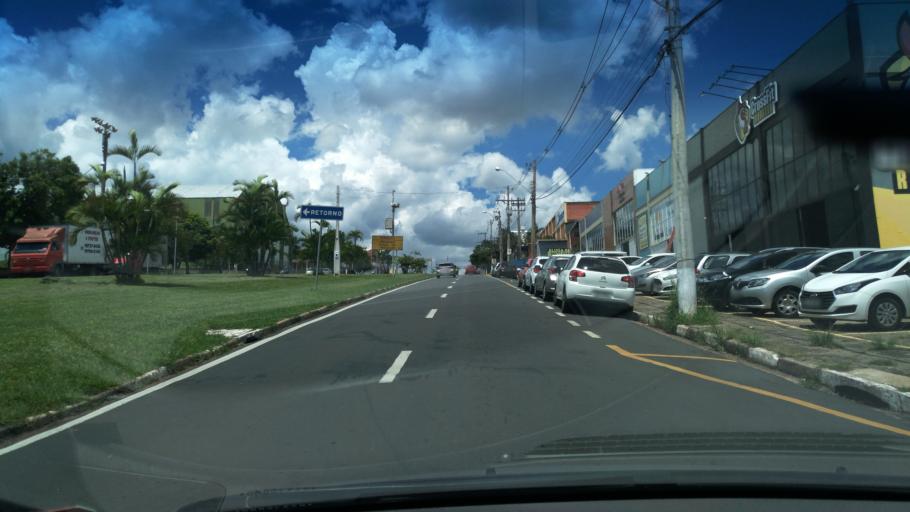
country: BR
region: Sao Paulo
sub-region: Vinhedo
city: Vinhedo
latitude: -23.0107
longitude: -46.9875
